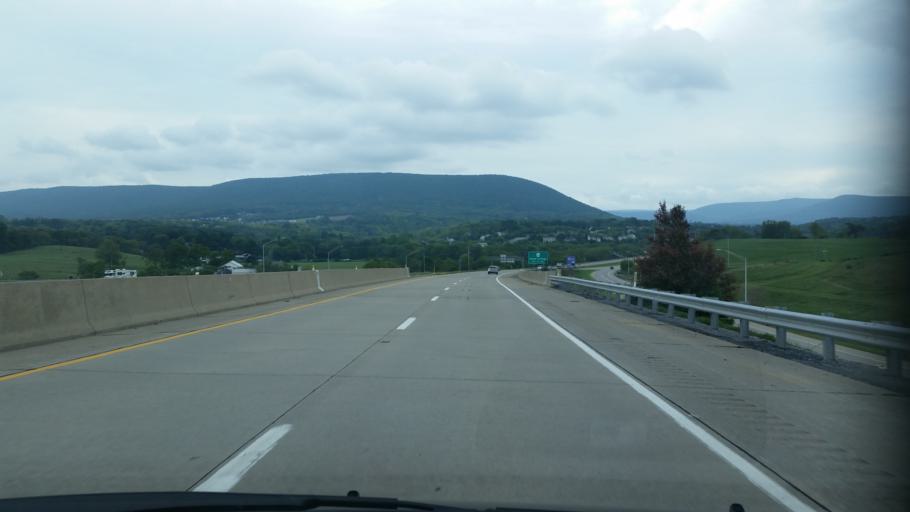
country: US
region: Pennsylvania
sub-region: Centre County
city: Houserville
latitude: 40.8235
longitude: -77.8426
